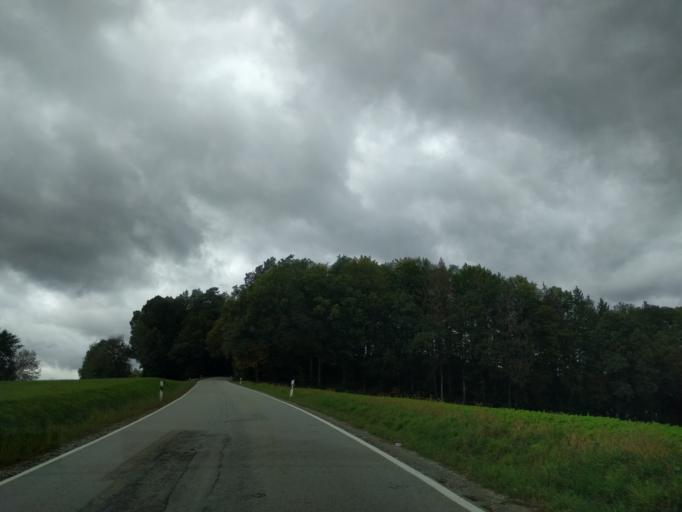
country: DE
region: Bavaria
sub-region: Lower Bavaria
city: Auerbach
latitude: 48.8141
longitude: 13.0814
